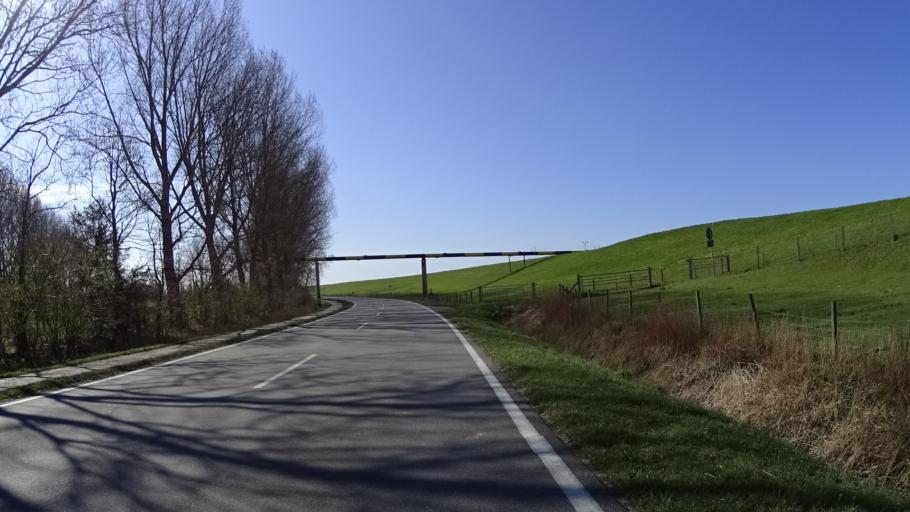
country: DE
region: Lower Saxony
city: Jemgum
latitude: 53.2841
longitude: 7.4045
